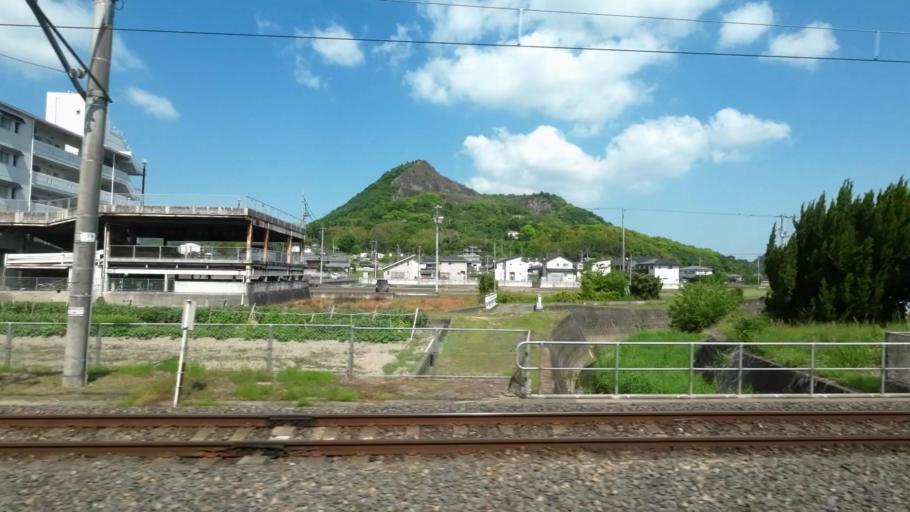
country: JP
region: Kagawa
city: Kan'onjicho
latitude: 34.1827
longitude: 133.7102
